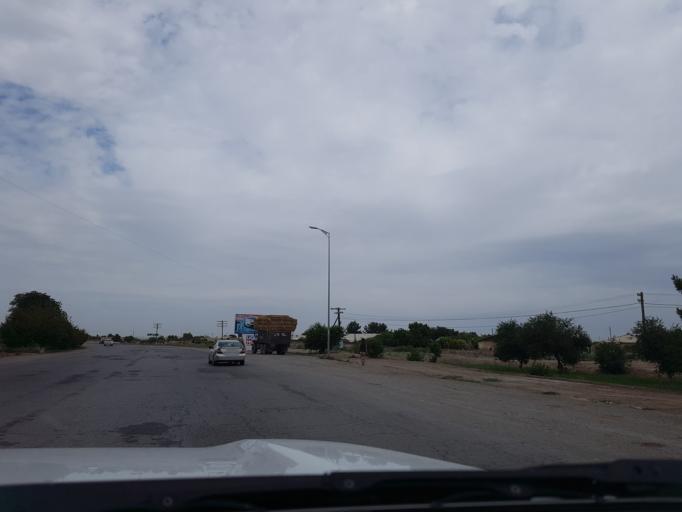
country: TM
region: Lebap
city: Turkmenabat
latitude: 38.9200
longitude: 63.7208
